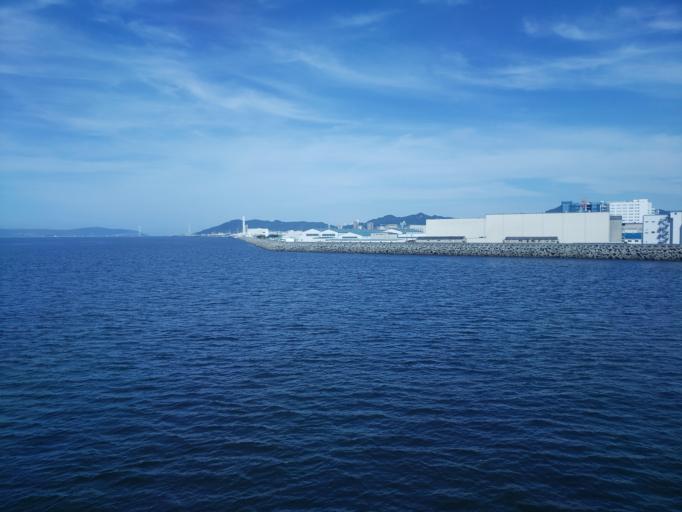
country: JP
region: Hyogo
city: Kobe
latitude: 34.6496
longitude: 135.1883
